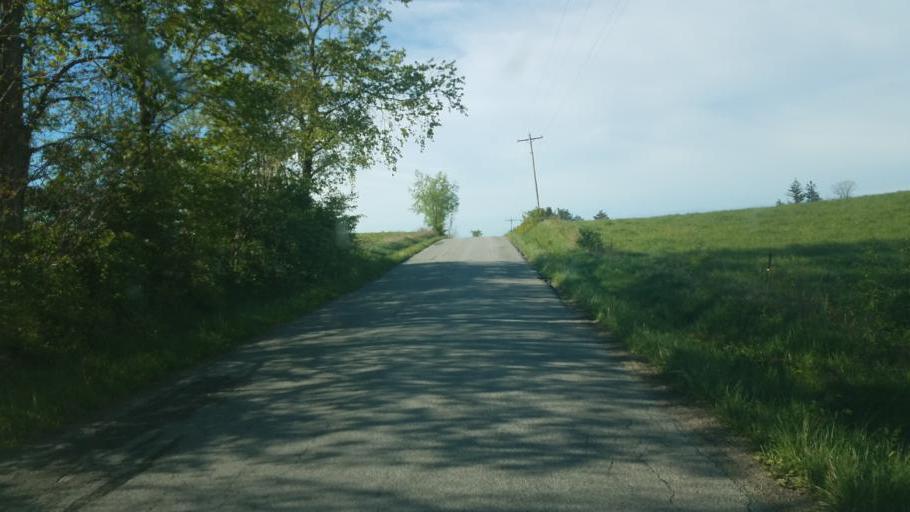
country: US
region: Ohio
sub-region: Morrow County
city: Mount Gilead
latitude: 40.5728
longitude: -82.8056
